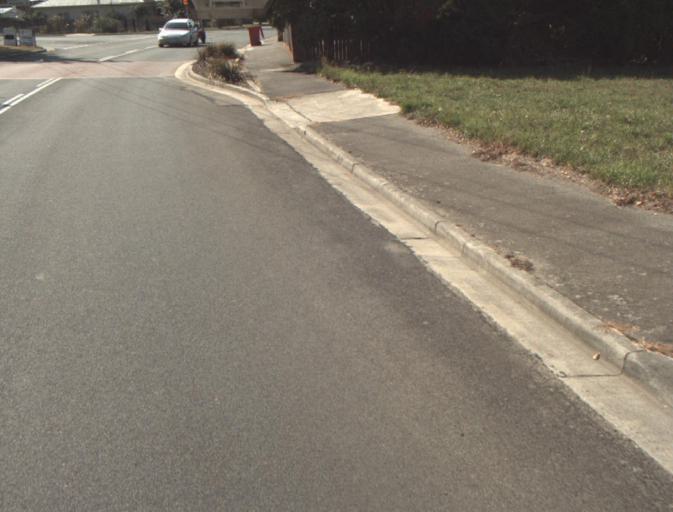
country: AU
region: Tasmania
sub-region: Launceston
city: Mayfield
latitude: -41.2542
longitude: 147.2157
